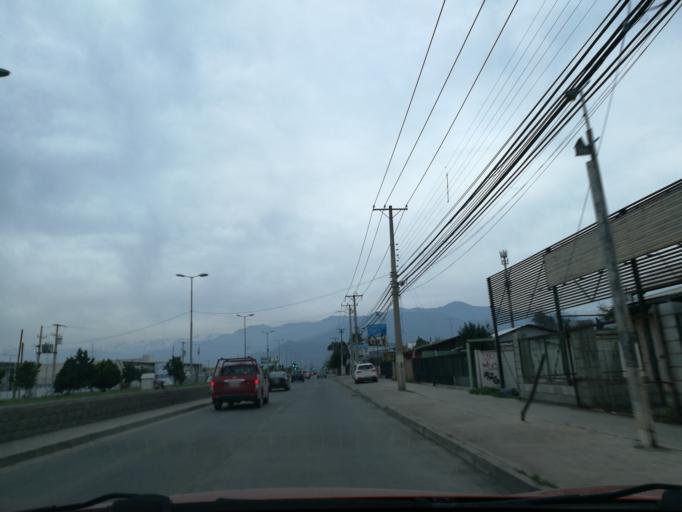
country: CL
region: O'Higgins
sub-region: Provincia de Cachapoal
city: Machali
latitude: -34.1753
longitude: -70.6927
